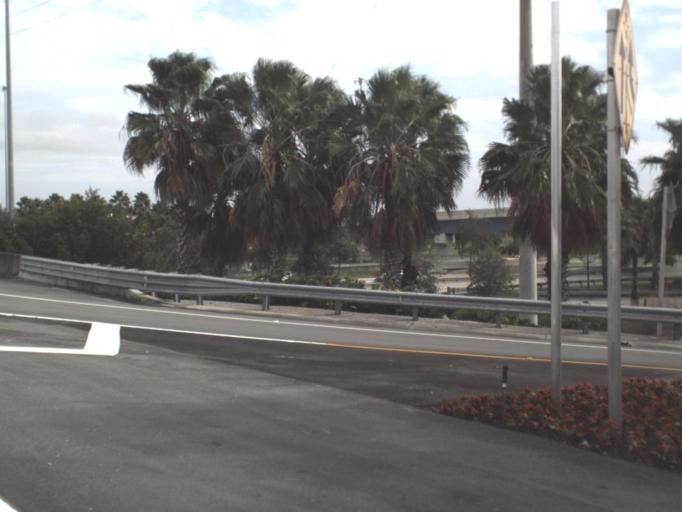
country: US
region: Florida
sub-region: Miami-Dade County
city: Brownsville
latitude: 25.7948
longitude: -80.2653
